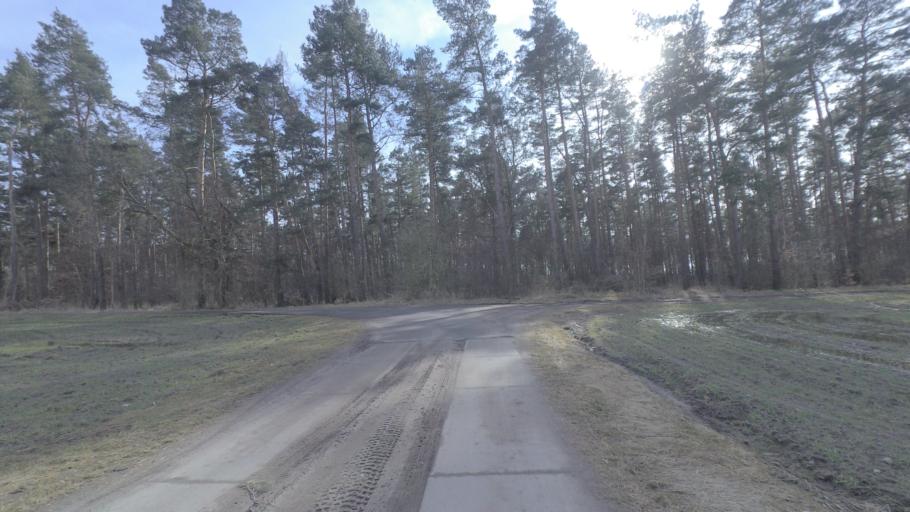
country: DE
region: Brandenburg
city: Ludwigsfelde
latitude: 52.2846
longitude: 13.2752
